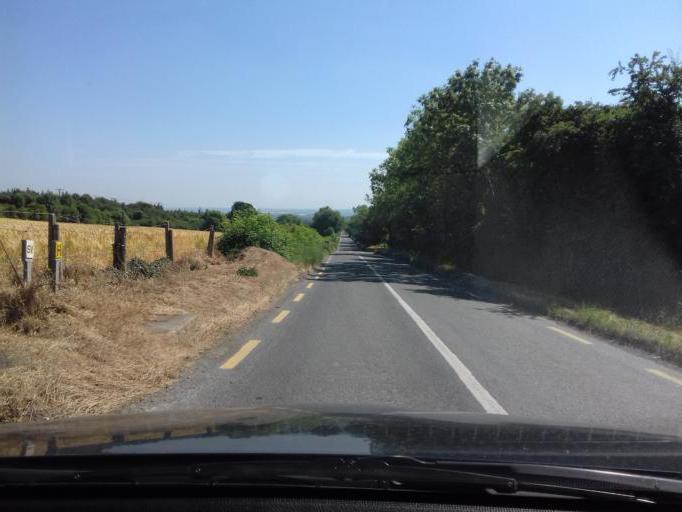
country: IE
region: Leinster
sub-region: An Mhi
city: Stamullin
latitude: 53.5582
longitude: -6.2724
